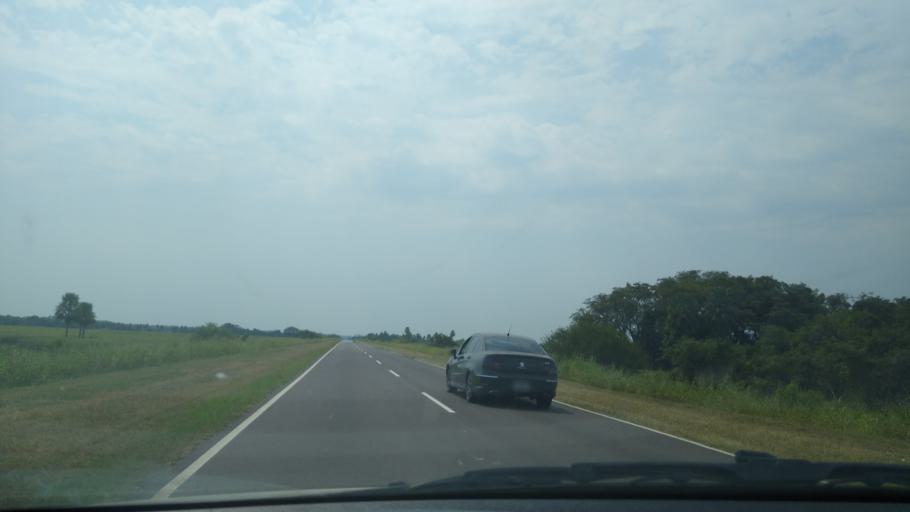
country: AR
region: Chaco
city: La Eduvigis
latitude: -27.0021
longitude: -58.9721
